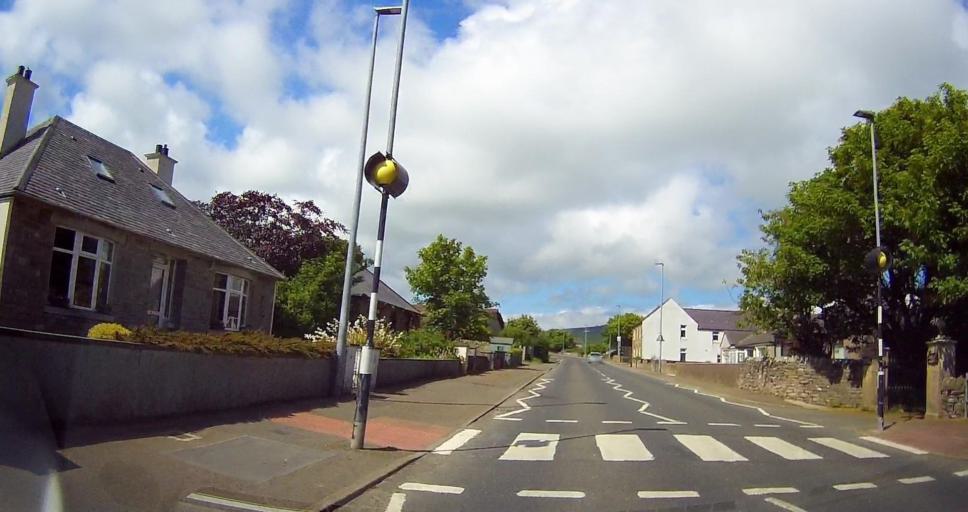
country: GB
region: Scotland
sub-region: Orkney Islands
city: Orkney
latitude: 58.9777
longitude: -2.9707
